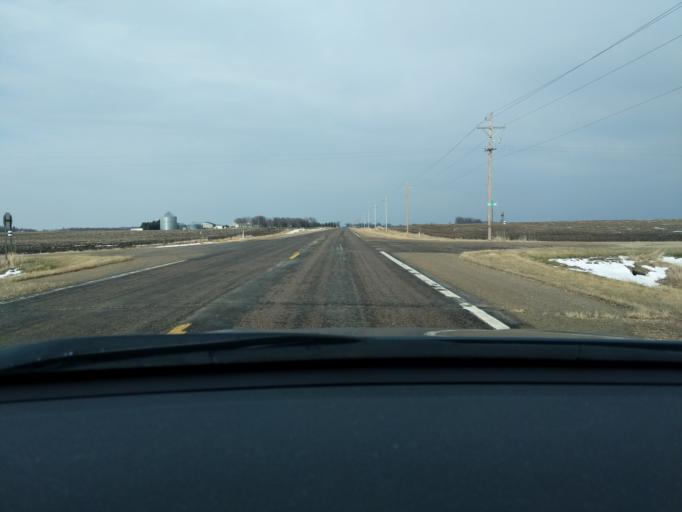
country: US
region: Minnesota
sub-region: Renville County
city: Renville
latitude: 44.7597
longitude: -95.3409
